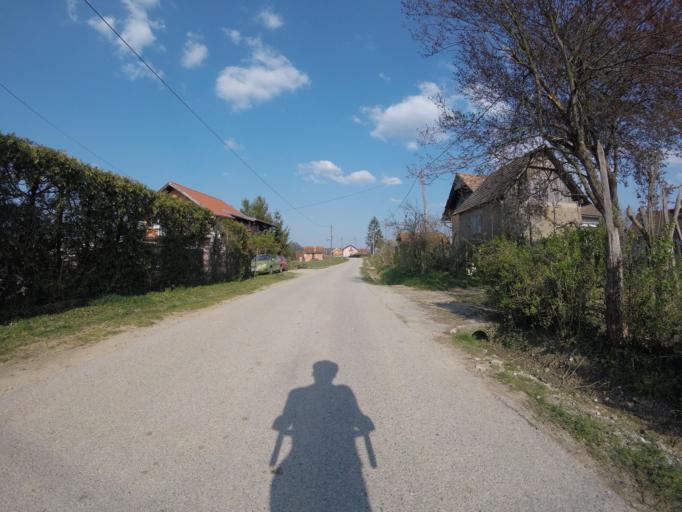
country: HR
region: Sisacko-Moslavacka
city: Glina
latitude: 45.5013
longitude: 15.9950
